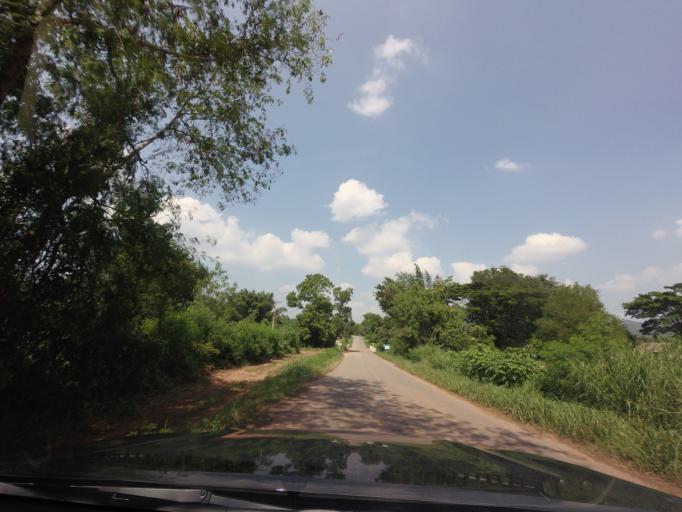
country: TH
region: Uttaradit
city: Fak Tha
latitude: 17.8956
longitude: 100.9771
